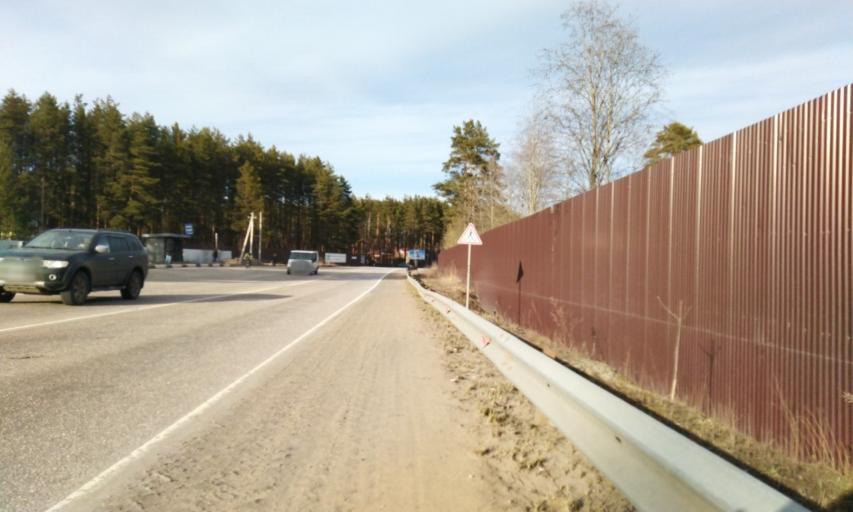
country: RU
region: Leningrad
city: Novoye Devyatkino
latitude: 60.1125
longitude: 30.4488
